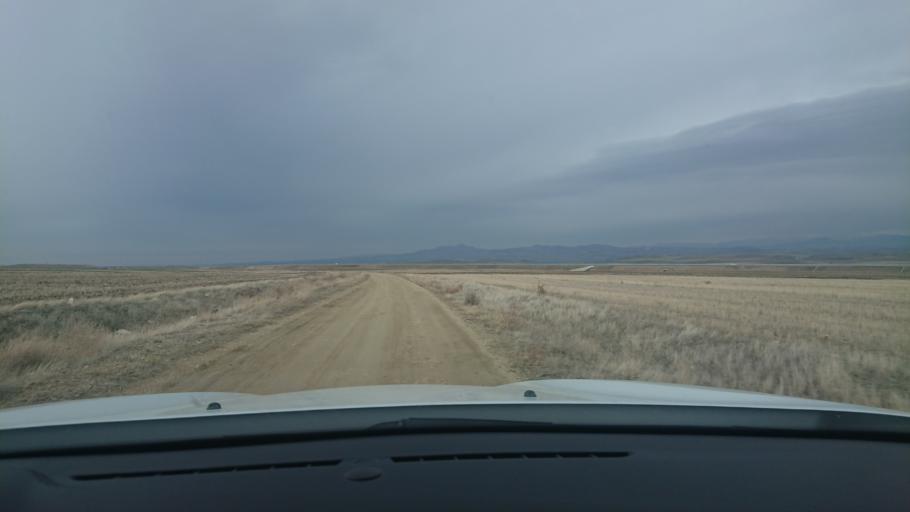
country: TR
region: Aksaray
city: Sariyahsi
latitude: 38.9823
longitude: 33.8773
